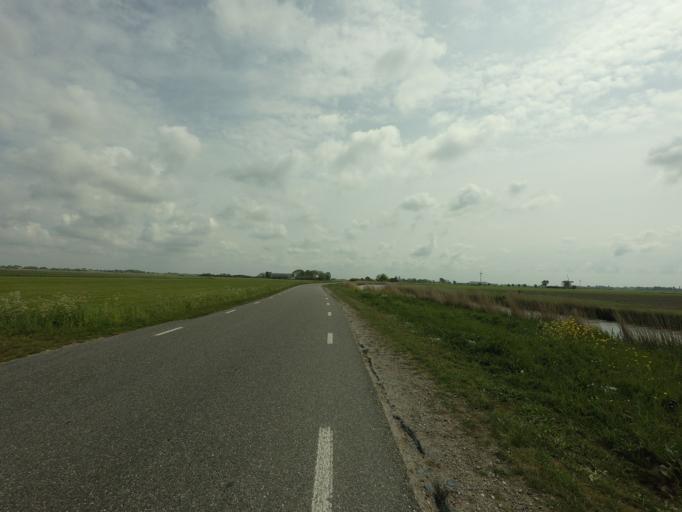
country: NL
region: Friesland
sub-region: Sudwest Fryslan
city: Bolsward
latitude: 53.1057
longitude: 5.5085
